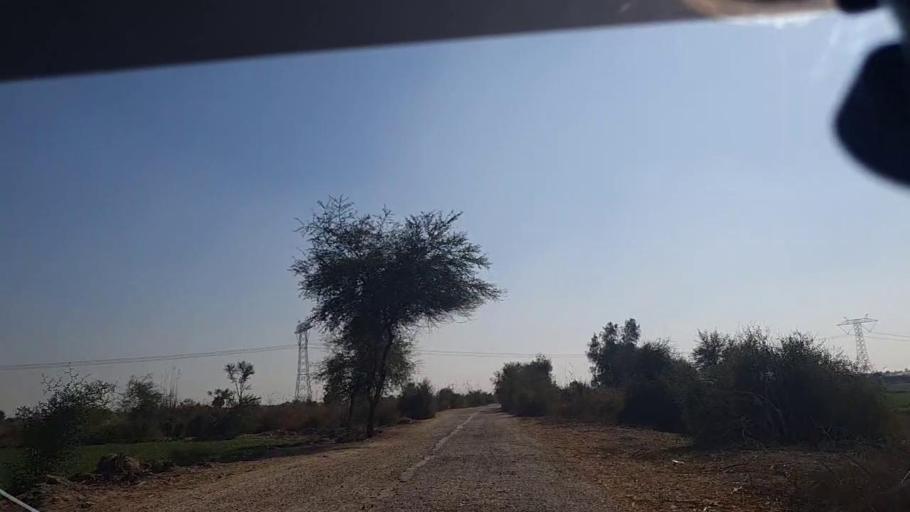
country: PK
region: Sindh
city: Khanpur
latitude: 27.5820
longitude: 69.3053
